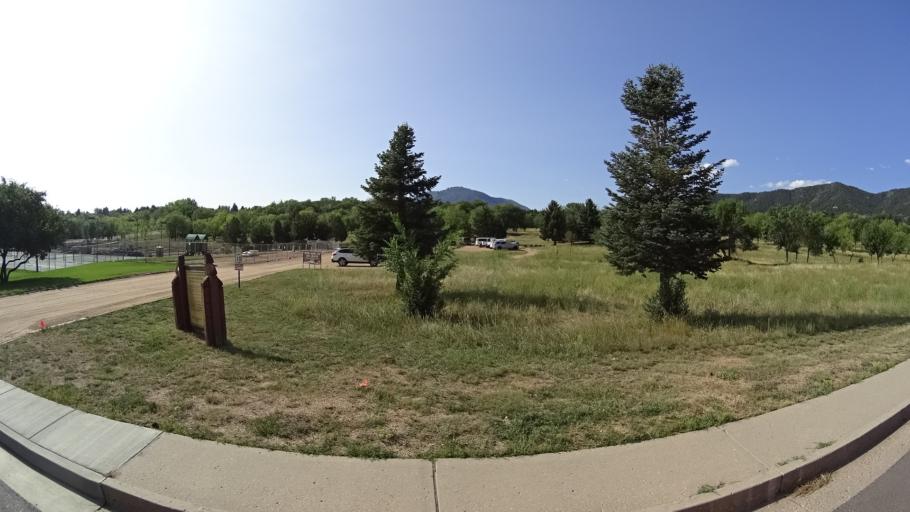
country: US
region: Colorado
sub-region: El Paso County
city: Colorado Springs
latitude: 38.8204
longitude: -104.8614
